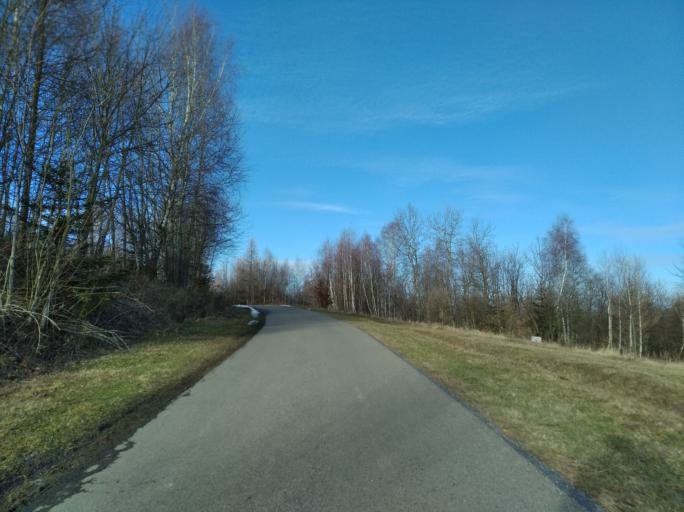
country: PL
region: Subcarpathian Voivodeship
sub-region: Powiat strzyzowski
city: Gwoznica Gorna
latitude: 49.8187
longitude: 21.9901
